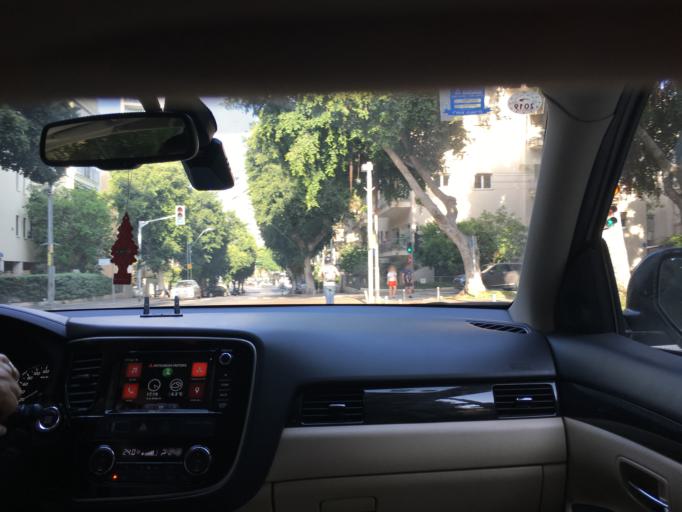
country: IL
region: Tel Aviv
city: Tel Aviv
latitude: 32.0758
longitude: 34.7798
